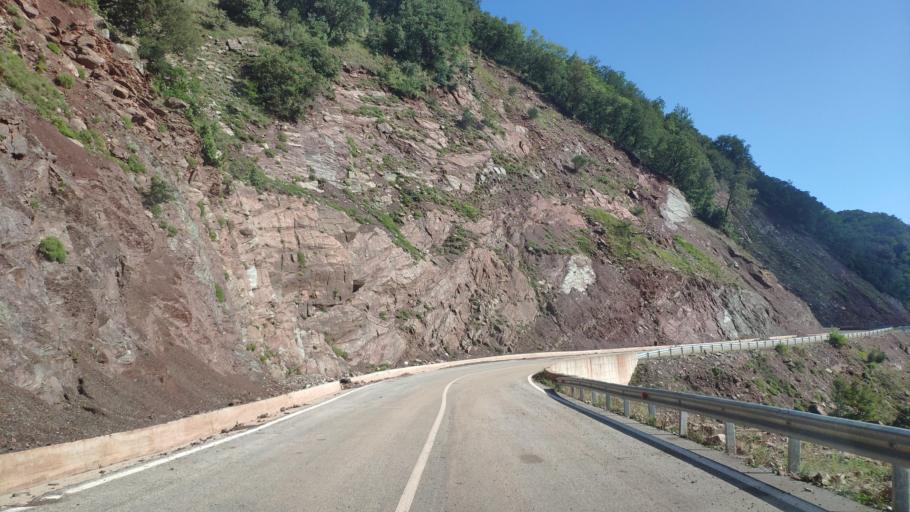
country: GR
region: Central Greece
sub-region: Nomos Evrytanias
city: Kerasochori
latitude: 39.1058
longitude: 21.6097
